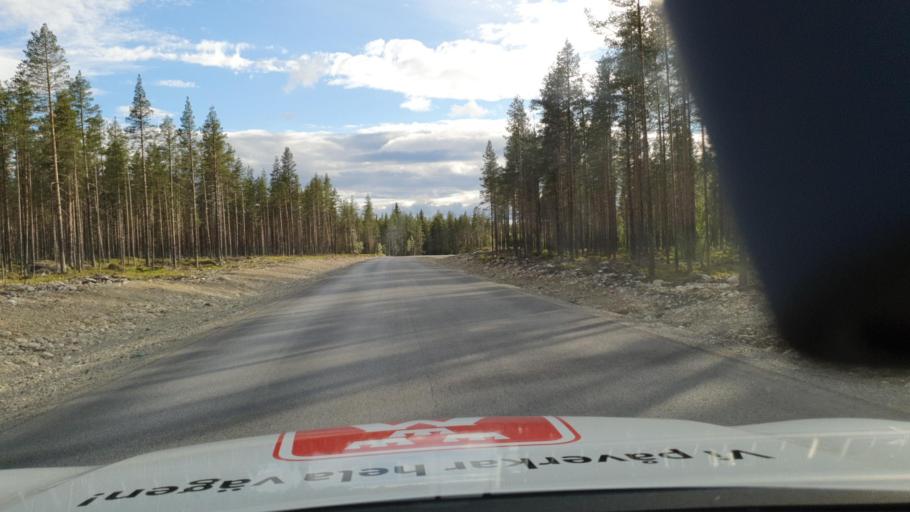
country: SE
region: Vaesterbotten
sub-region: Storumans Kommun
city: Storuman
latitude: 65.0739
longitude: 17.1105
